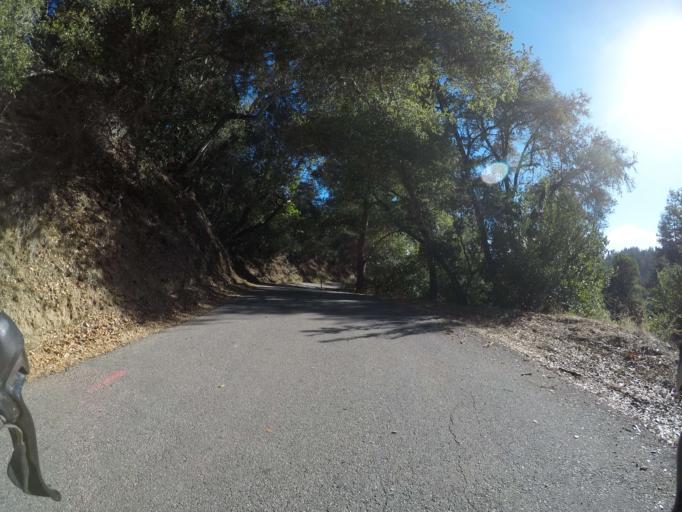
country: US
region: California
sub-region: Santa Cruz County
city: Scotts Valley
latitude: 37.0998
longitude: -121.9925
